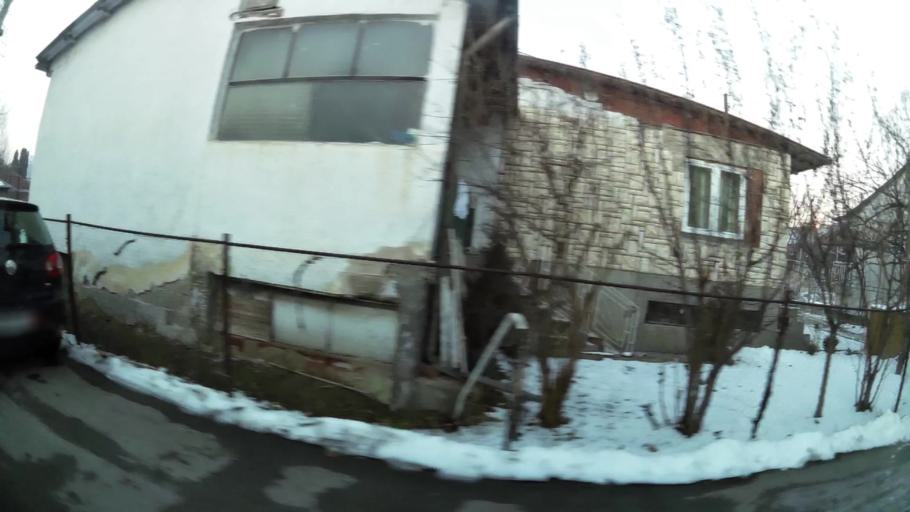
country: MK
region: Kisela Voda
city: Usje
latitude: 41.9805
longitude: 21.4851
